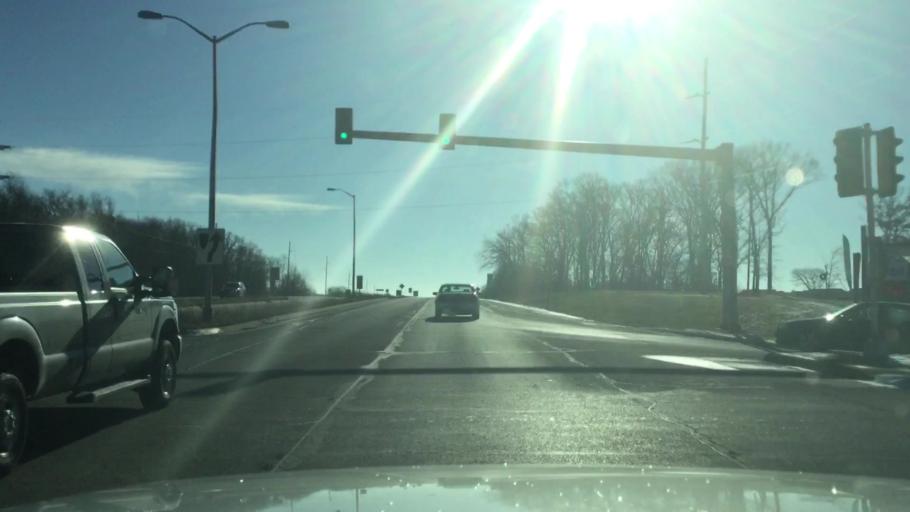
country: US
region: Wisconsin
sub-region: Racine County
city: Rochester
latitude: 42.7414
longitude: -88.2159
